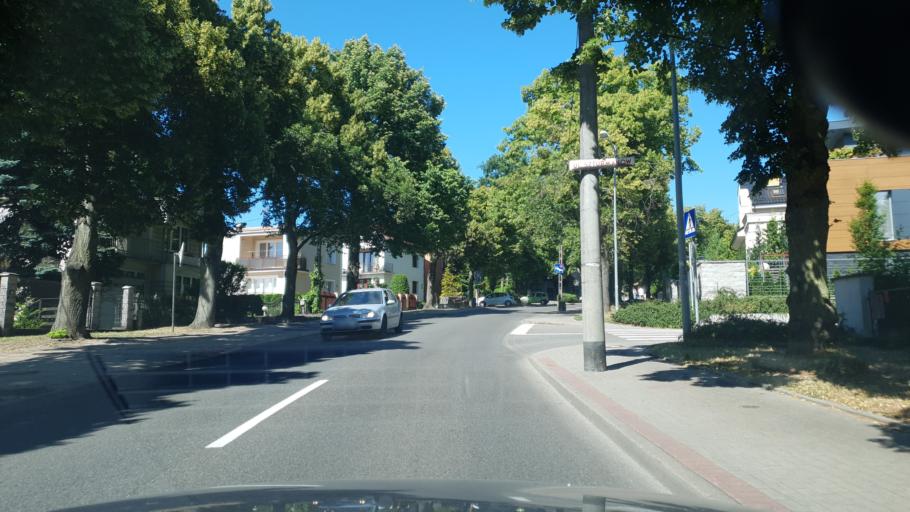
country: PL
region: Pomeranian Voivodeship
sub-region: Gdynia
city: Gdynia
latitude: 54.4869
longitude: 18.5469
